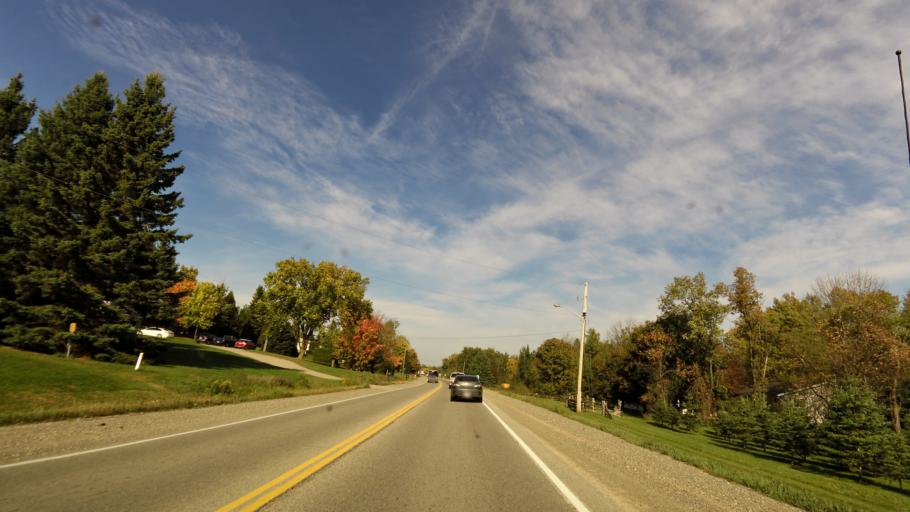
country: CA
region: Ontario
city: Orangeville
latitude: 43.7592
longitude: -80.0623
